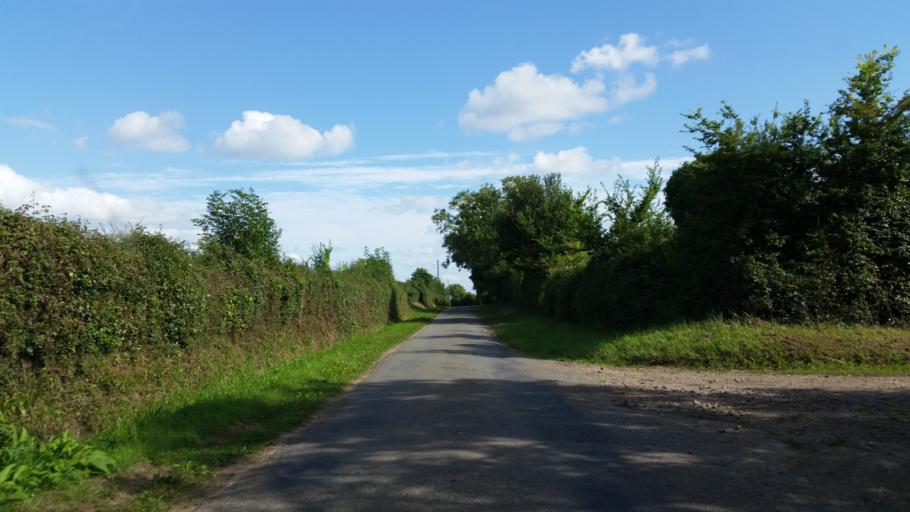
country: FR
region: Lower Normandy
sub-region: Departement de la Manche
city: Sainte-Mere-Eglise
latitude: 49.4616
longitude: -1.3011
